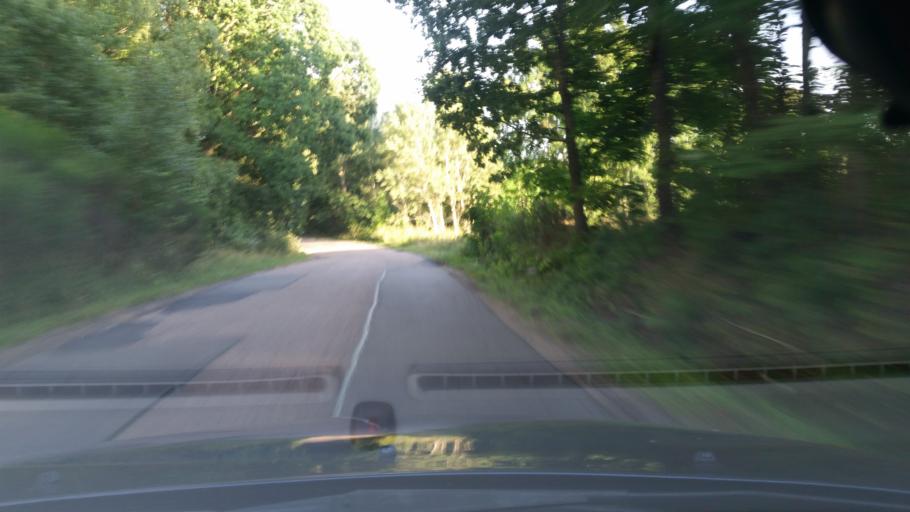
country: PL
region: Pomeranian Voivodeship
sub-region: Powiat wejherowski
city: Choczewo
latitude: 54.7585
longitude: 17.7752
